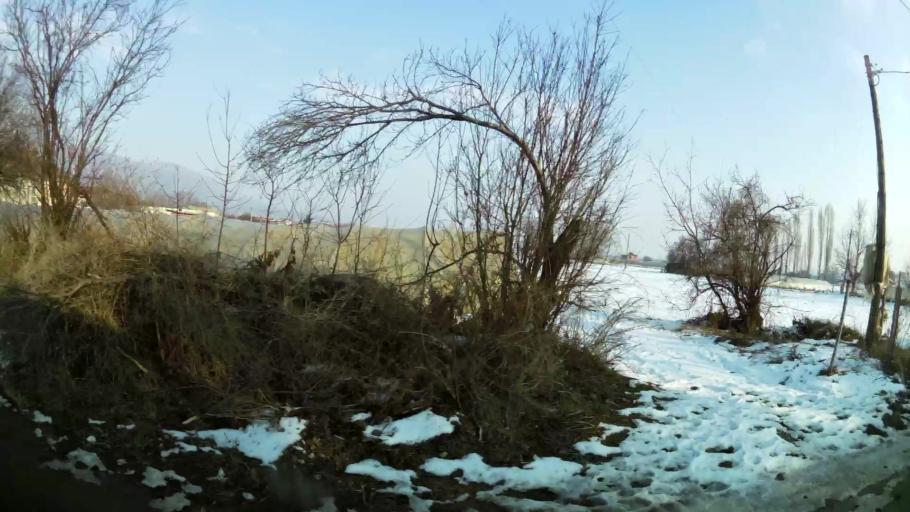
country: MK
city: Creshevo
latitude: 42.0265
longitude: 21.5200
